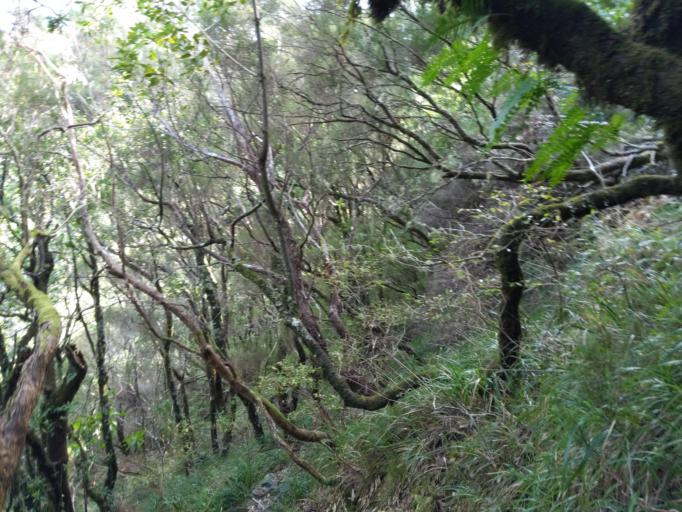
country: PT
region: Madeira
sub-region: Calheta
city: Arco da Calheta
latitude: 32.7637
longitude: -17.1300
